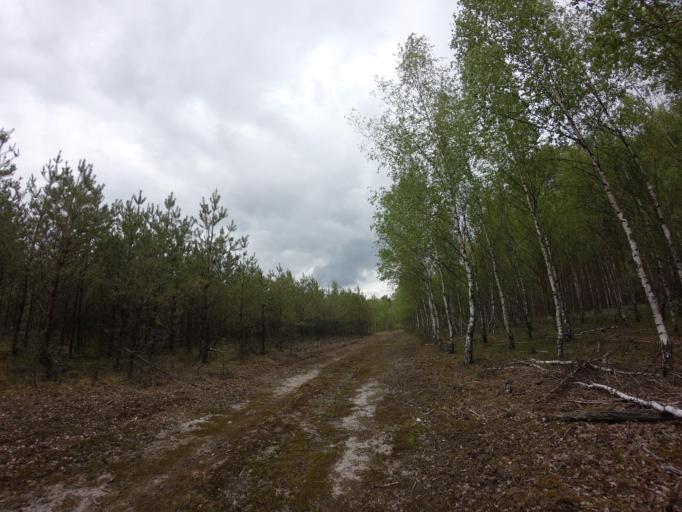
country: PL
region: West Pomeranian Voivodeship
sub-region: Powiat drawski
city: Kalisz Pomorski
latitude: 53.1908
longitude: 15.9806
